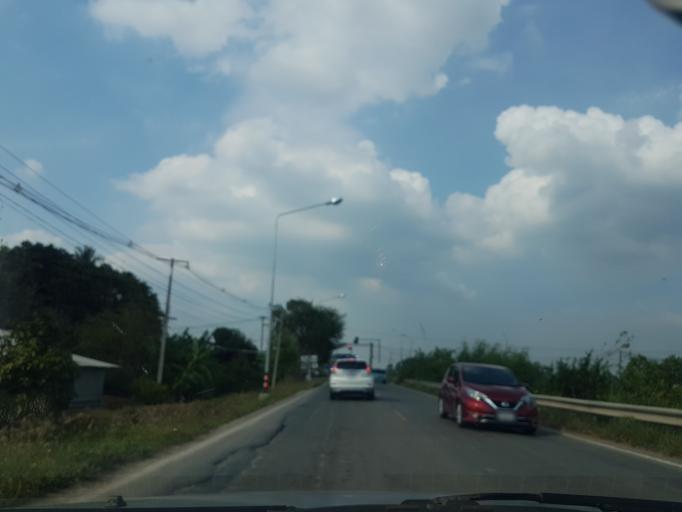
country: TH
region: Phra Nakhon Si Ayutthaya
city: Phachi
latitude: 14.4173
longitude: 100.7821
